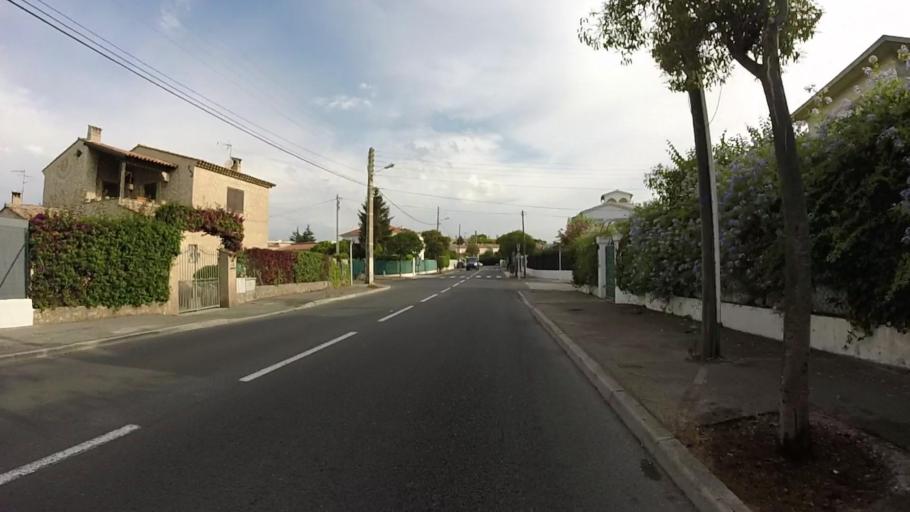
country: FR
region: Provence-Alpes-Cote d'Azur
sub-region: Departement des Alpes-Maritimes
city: Antibes
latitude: 43.5862
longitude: 7.1072
